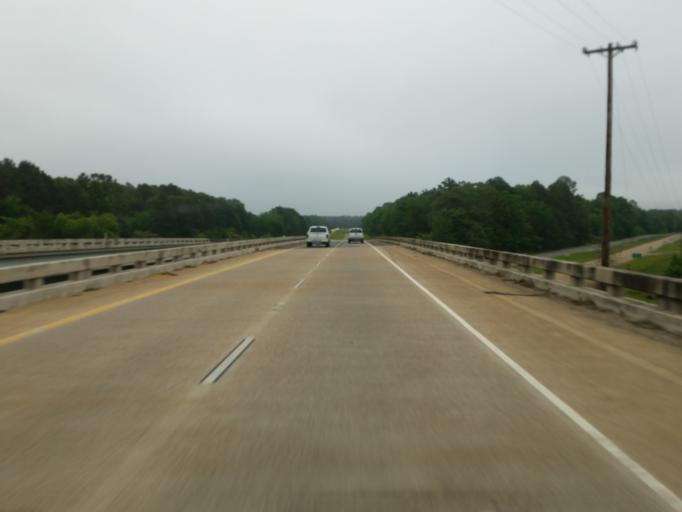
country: US
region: Louisiana
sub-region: Bossier Parish
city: Haughton
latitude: 32.5658
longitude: -93.4927
